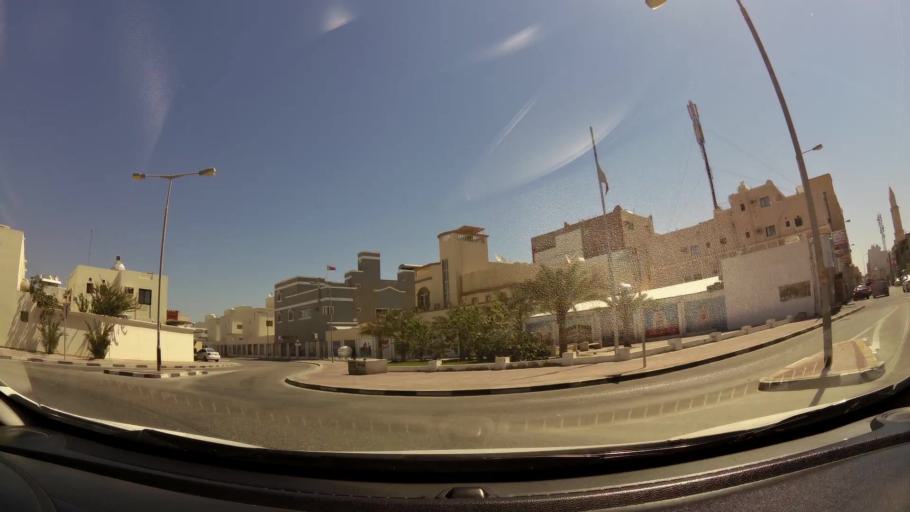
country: BH
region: Muharraq
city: Al Muharraq
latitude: 26.2721
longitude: 50.6092
